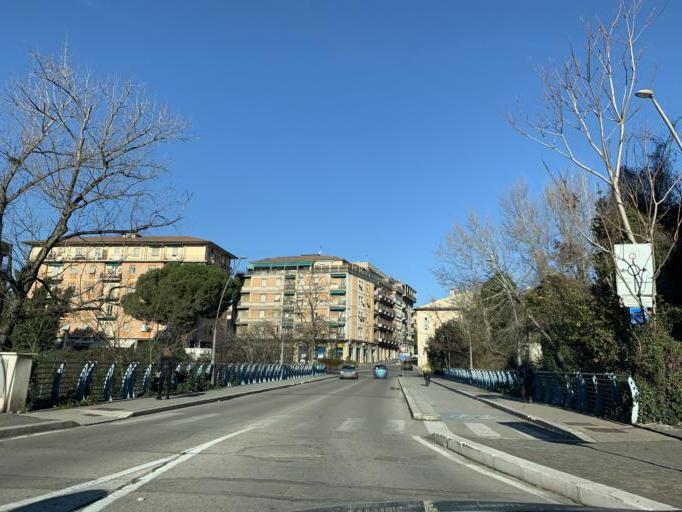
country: IT
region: Umbria
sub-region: Provincia di Terni
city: Terni
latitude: 42.5606
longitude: 12.6516
